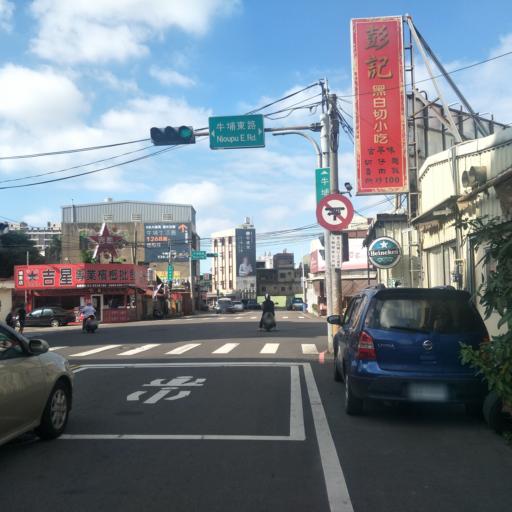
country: TW
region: Taiwan
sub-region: Hsinchu
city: Hsinchu
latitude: 24.7950
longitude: 120.9415
